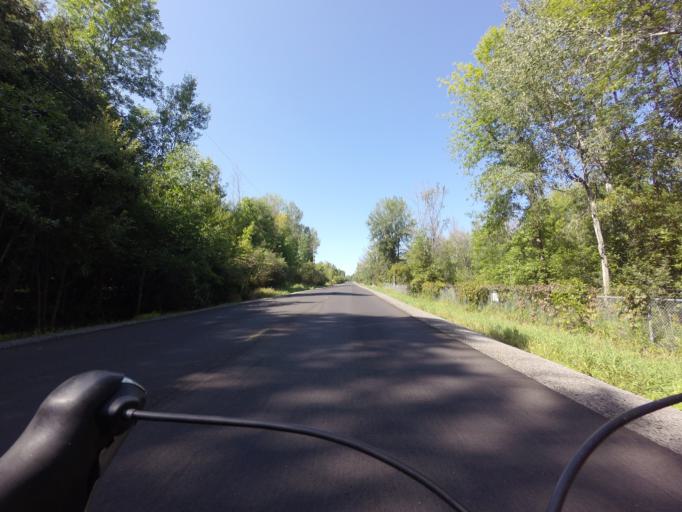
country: CA
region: Ontario
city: Bells Corners
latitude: 45.3790
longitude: -75.9394
